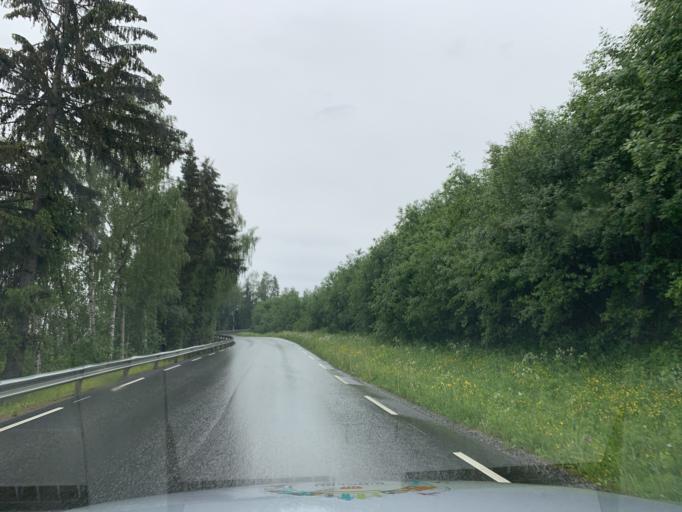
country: NO
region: Oppland
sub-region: Ringebu
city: Ringebu
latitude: 61.4466
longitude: 10.1855
